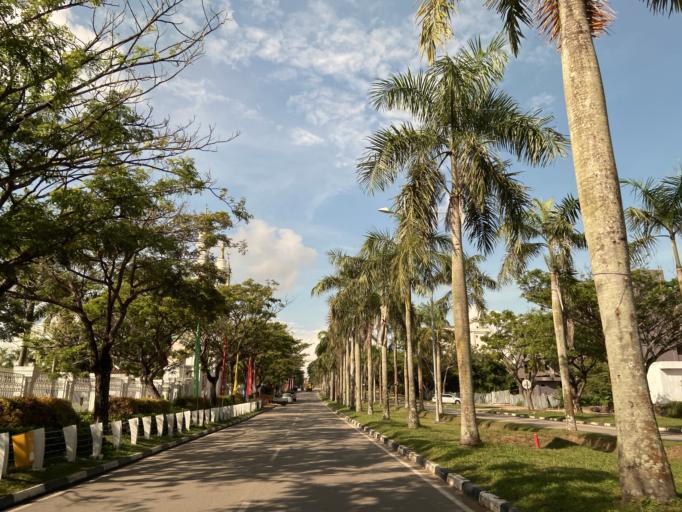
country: SG
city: Singapore
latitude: 1.1294
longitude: 104.0530
